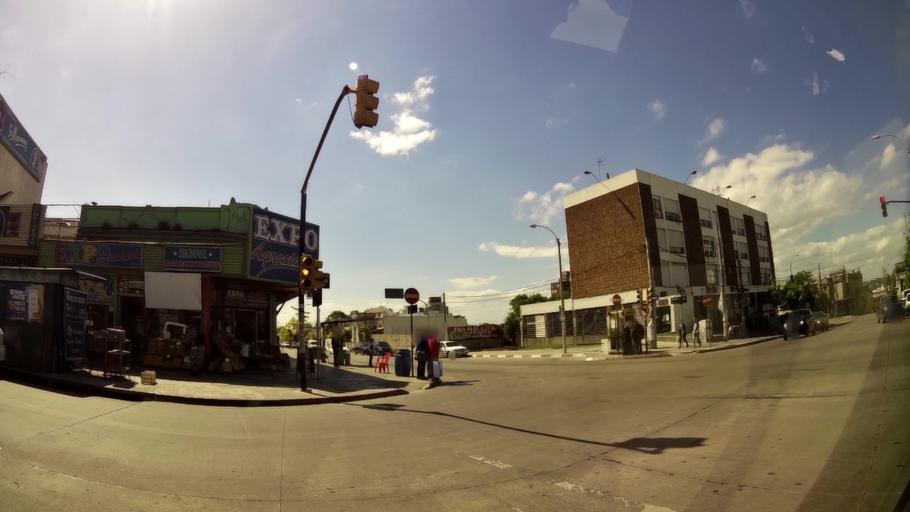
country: UY
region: Montevideo
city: Montevideo
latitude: -34.8551
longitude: -56.2222
